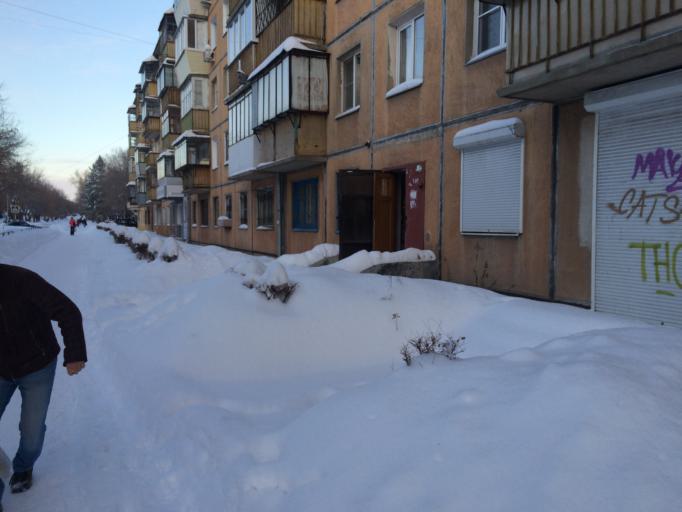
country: RU
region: Chelyabinsk
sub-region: Gorod Magnitogorsk
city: Magnitogorsk
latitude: 53.3999
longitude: 58.9717
